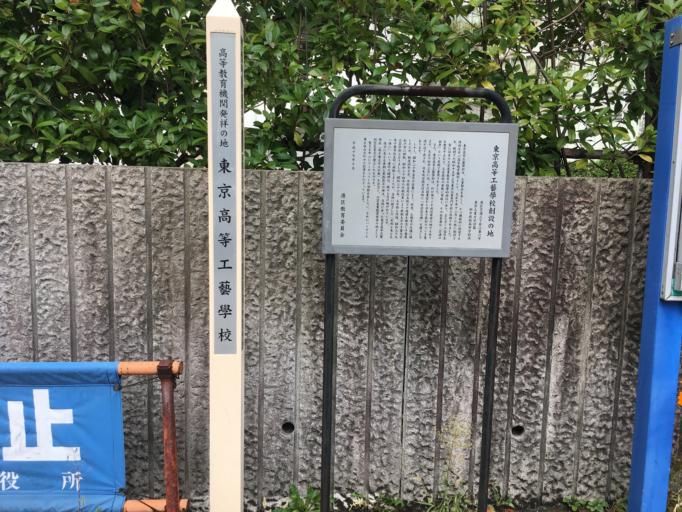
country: JP
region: Tokyo
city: Tokyo
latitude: 35.6440
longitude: 139.7486
